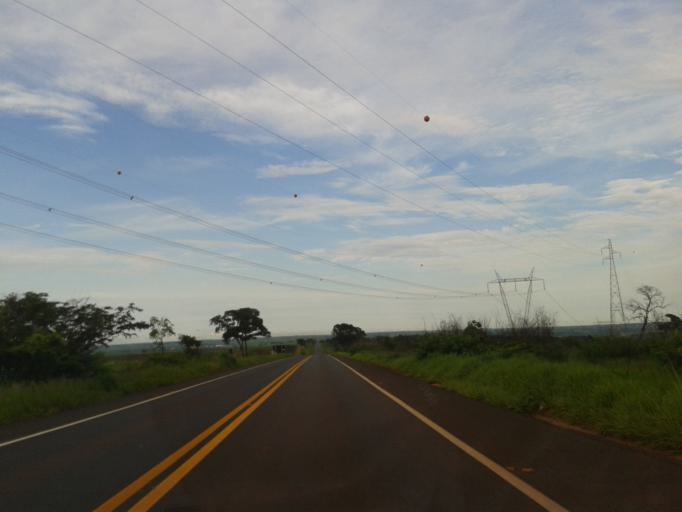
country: BR
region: Minas Gerais
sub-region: Santa Vitoria
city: Santa Vitoria
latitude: -19.0429
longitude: -50.4345
